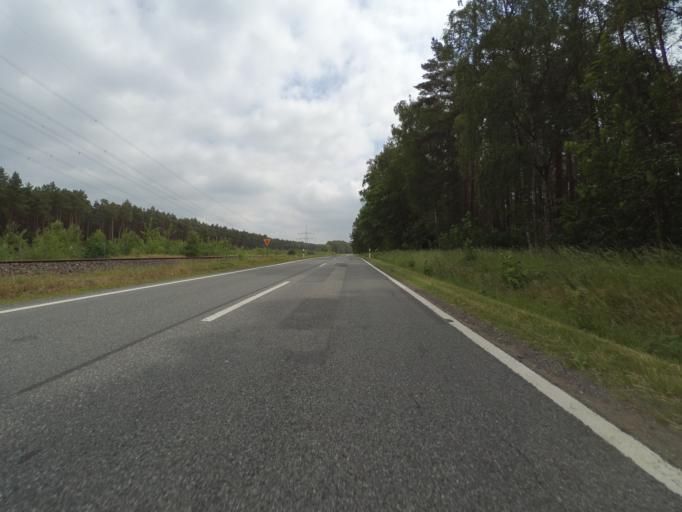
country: DE
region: Mecklenburg-Vorpommern
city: Malchow
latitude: 53.5319
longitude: 12.4939
